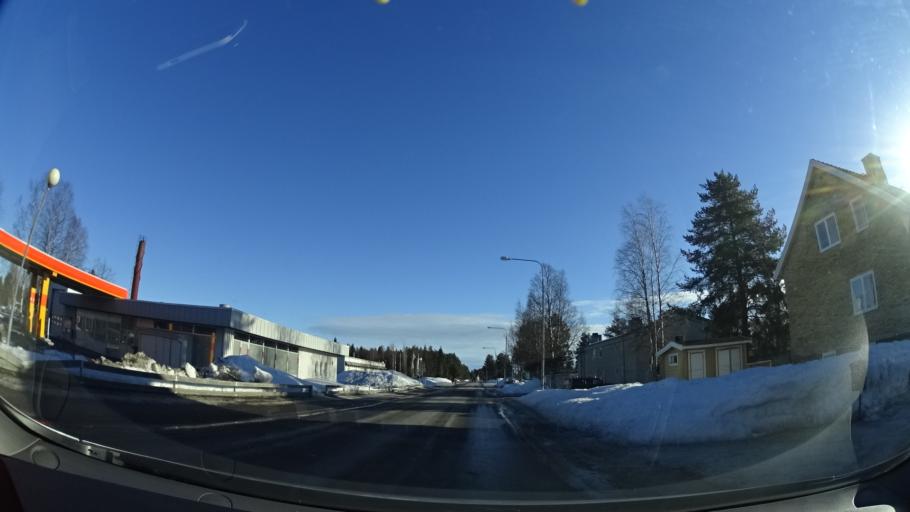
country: SE
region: Vaesterbotten
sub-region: Skelleftea Kommun
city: Byske
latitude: 64.9564
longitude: 21.2091
